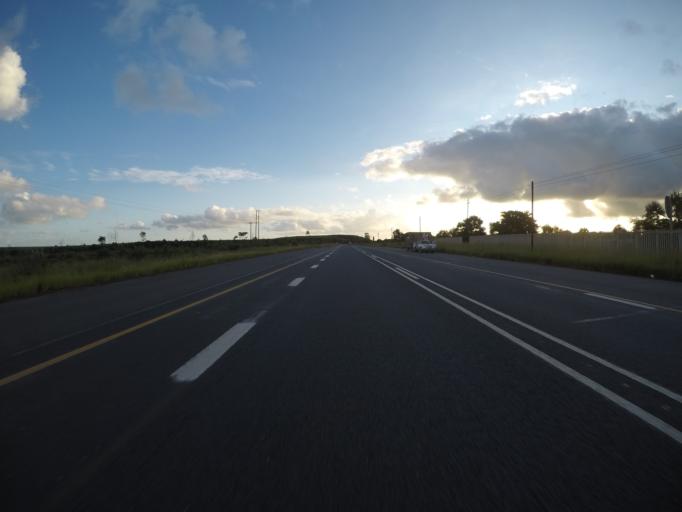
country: ZA
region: KwaZulu-Natal
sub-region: uThungulu District Municipality
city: KwaMbonambi
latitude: -28.6058
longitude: 32.0927
